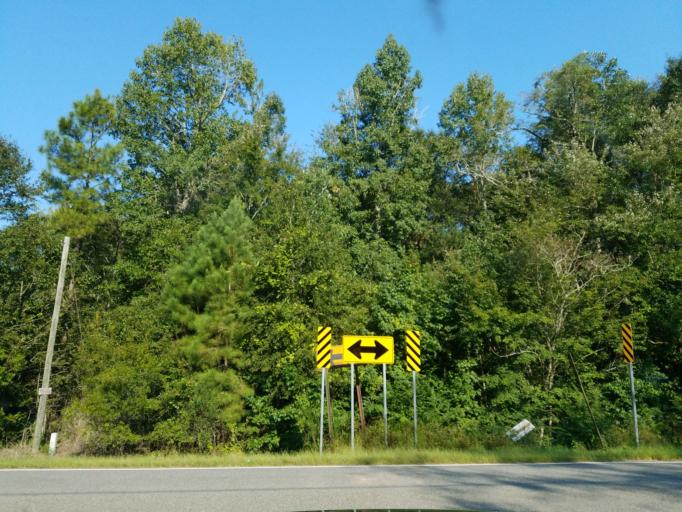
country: US
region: Georgia
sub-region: Lowndes County
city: Hahira
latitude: 31.0081
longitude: -83.3880
